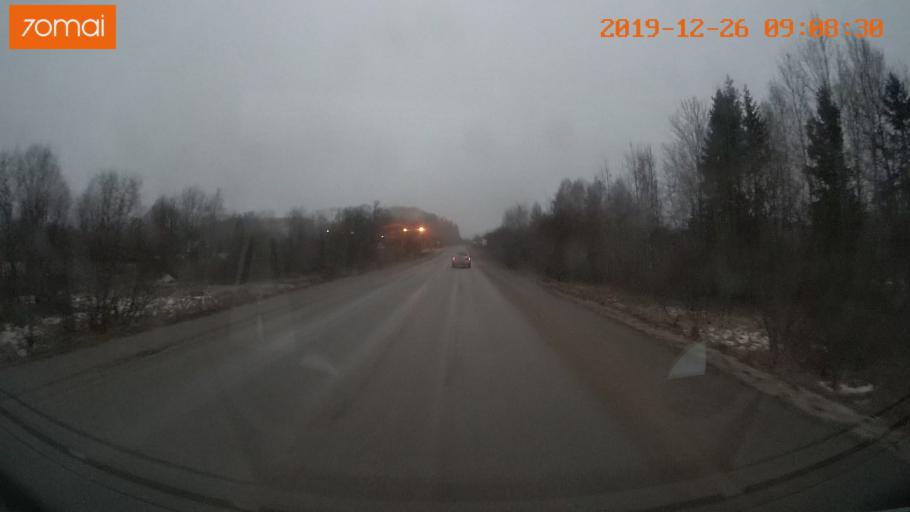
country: RU
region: Vologda
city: Gryazovets
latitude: 58.8573
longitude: 40.2482
